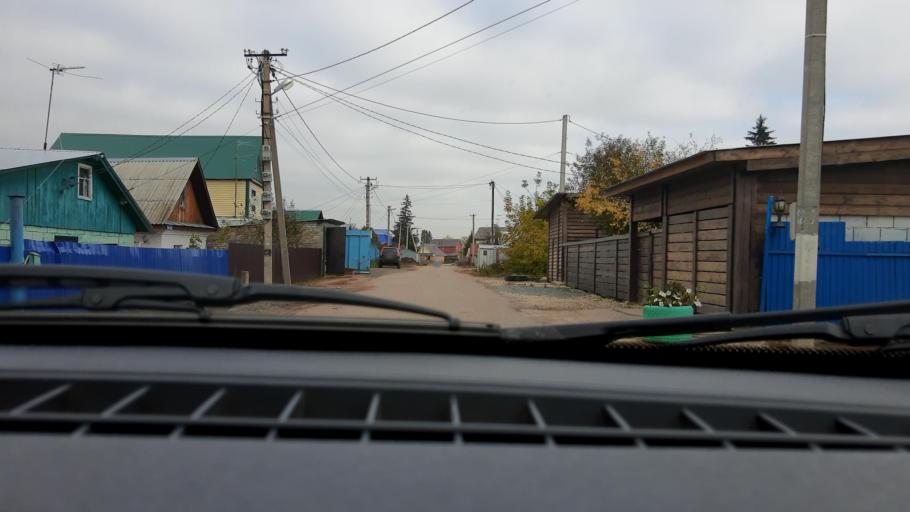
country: RU
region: Bashkortostan
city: Mikhaylovka
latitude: 54.7926
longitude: 55.8829
